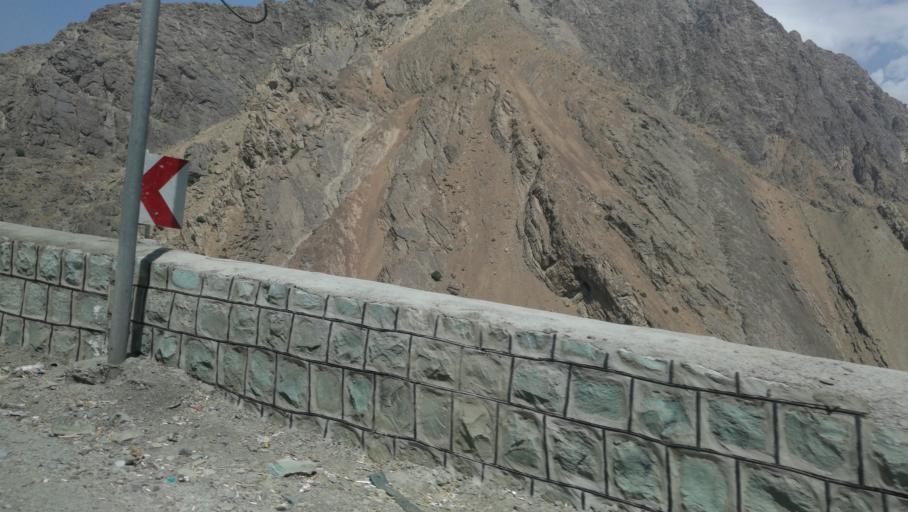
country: IR
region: Alborz
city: Karaj
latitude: 35.9501
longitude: 51.0875
